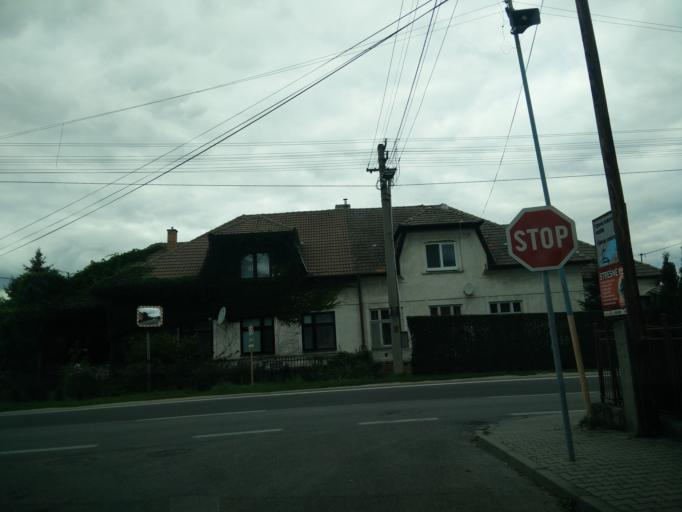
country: SK
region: Nitriansky
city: Partizanske
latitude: 48.6333
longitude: 18.4732
